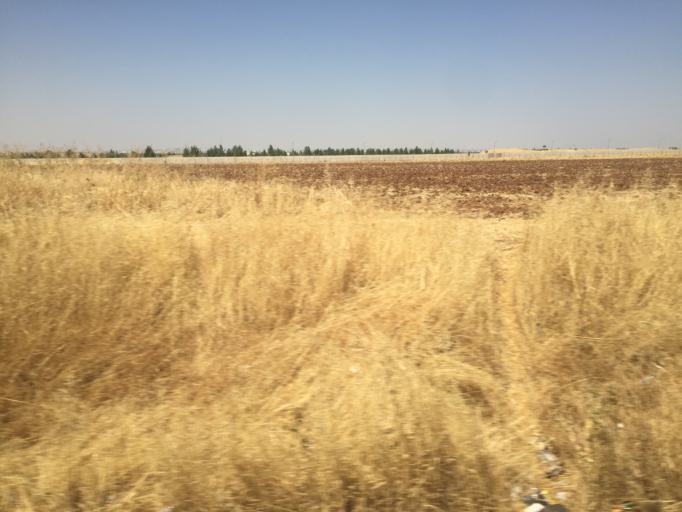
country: TR
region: Diyarbakir
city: Diyarbakir
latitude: 37.8724
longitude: 40.2180
